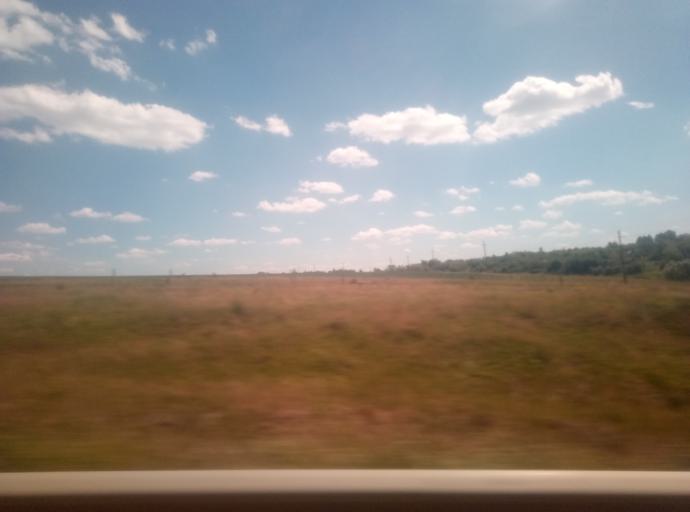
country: RU
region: Tula
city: Kireyevsk
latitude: 53.9392
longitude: 37.9484
